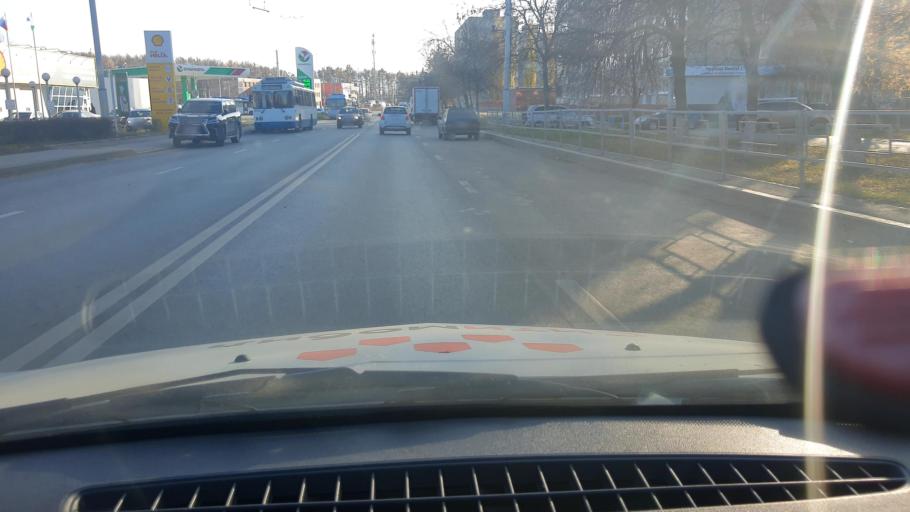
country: RU
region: Bashkortostan
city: Ufa
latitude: 54.6994
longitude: 56.0067
